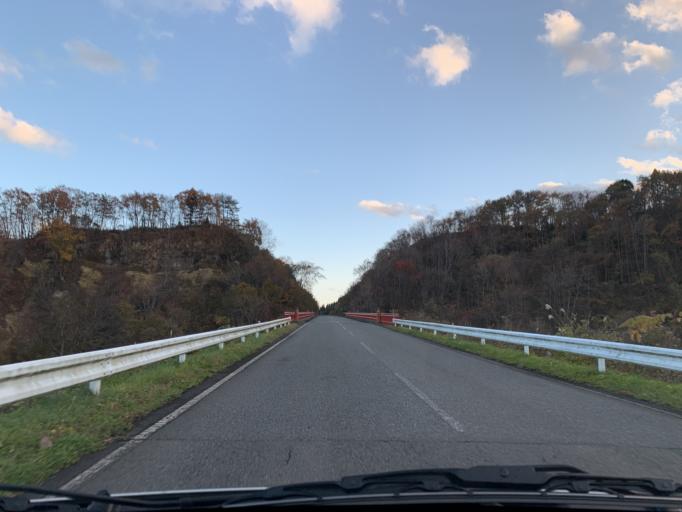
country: JP
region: Iwate
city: Ichinoseki
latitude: 39.0194
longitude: 141.0229
